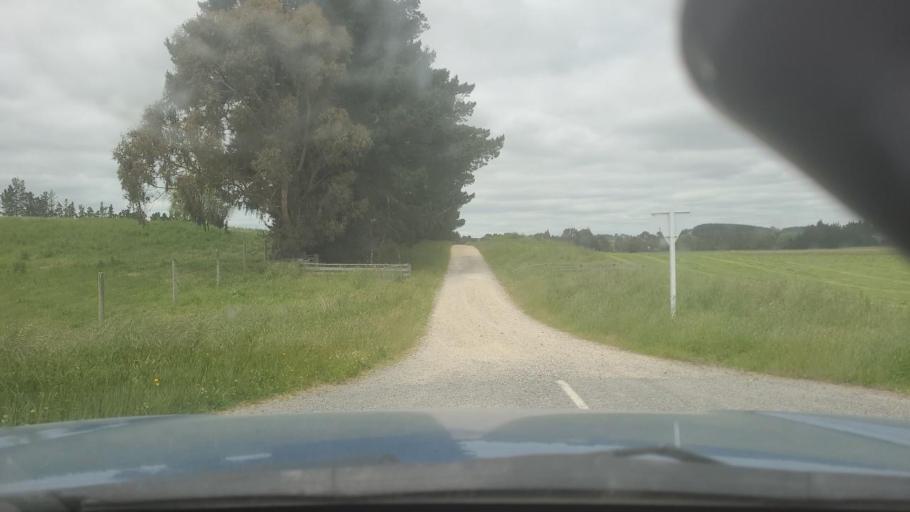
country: NZ
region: Southland
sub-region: Gore District
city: Gore
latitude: -46.1882
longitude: 168.6592
